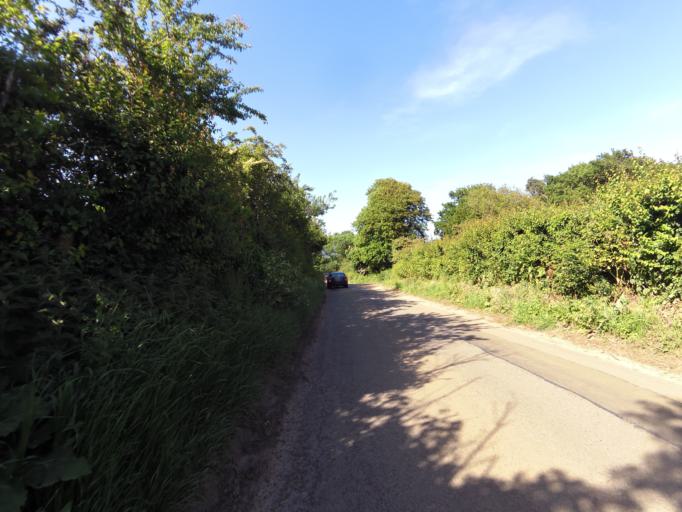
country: GB
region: England
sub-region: Suffolk
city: Felixstowe
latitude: 51.9997
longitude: 1.4144
